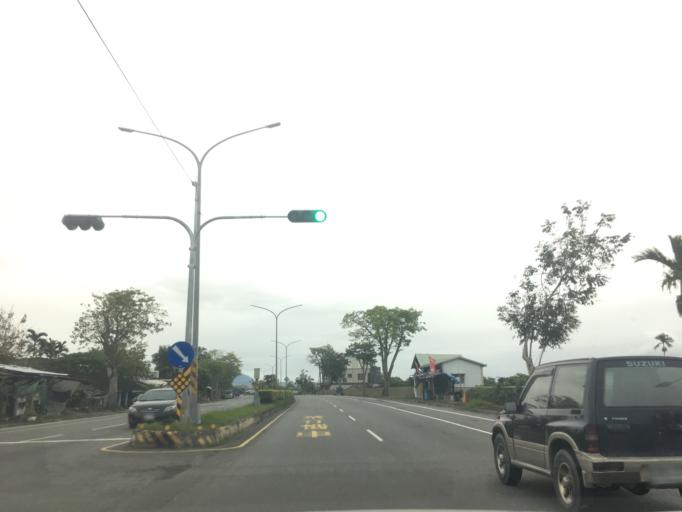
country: TW
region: Taiwan
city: Taitung City
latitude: 22.7171
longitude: 121.0504
